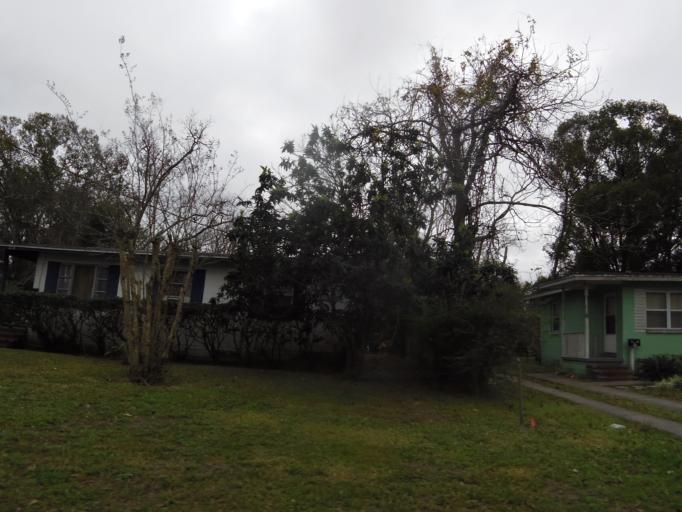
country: US
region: Florida
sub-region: Duval County
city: Jacksonville
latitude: 30.3684
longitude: -81.7166
